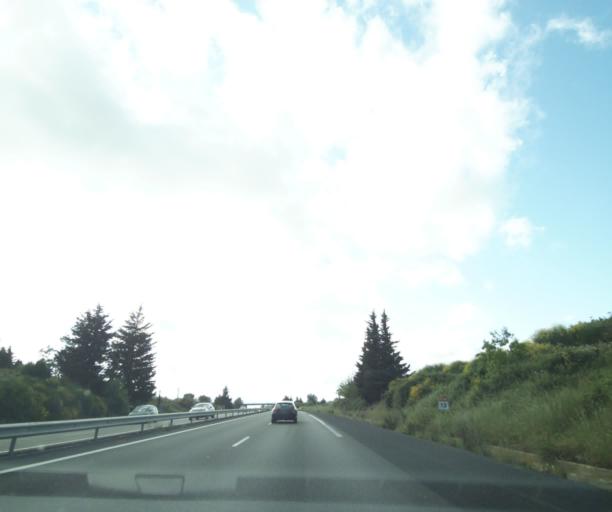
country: FR
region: Languedoc-Roussillon
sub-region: Departement du Gard
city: Garons
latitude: 43.7401
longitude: 4.4564
